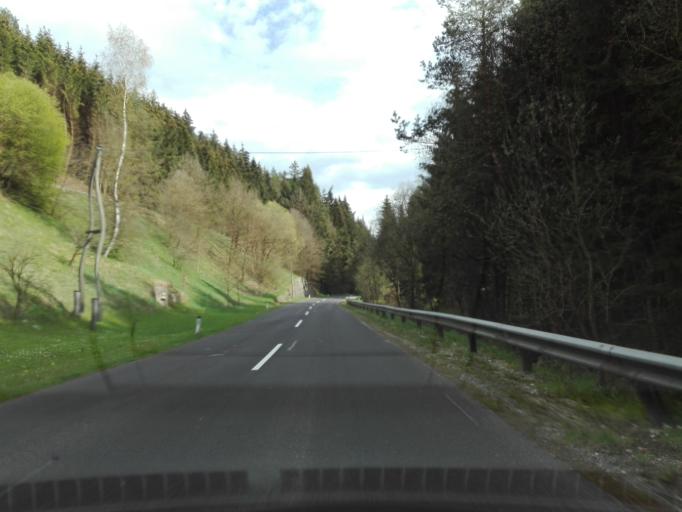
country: AT
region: Upper Austria
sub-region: Politischer Bezirk Rohrbach
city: Kleinzell im Muehlkreis
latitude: 48.4751
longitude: 14.0098
